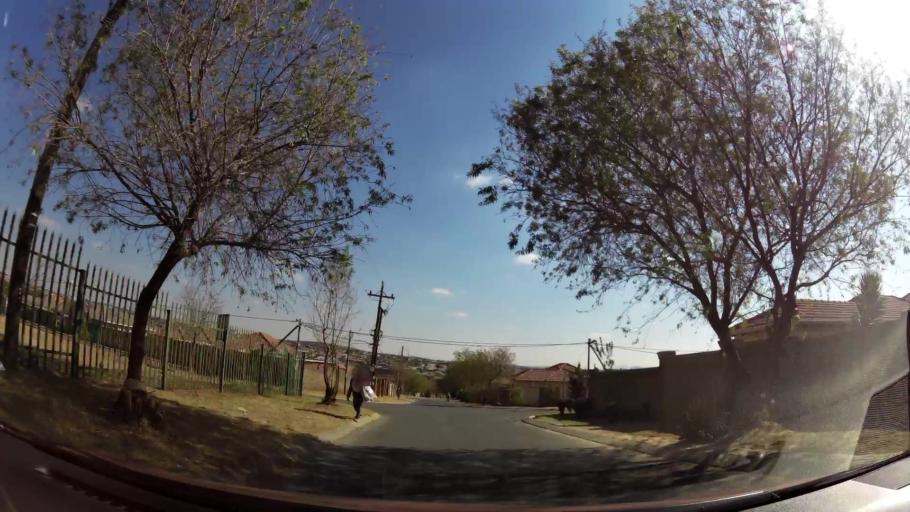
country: ZA
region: Gauteng
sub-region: West Rand District Municipality
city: Muldersdriseloop
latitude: -26.0264
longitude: 27.9367
